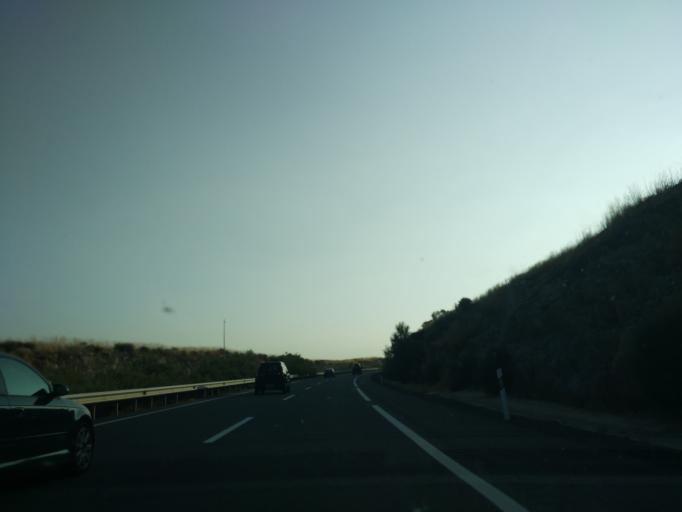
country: ES
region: Castille and Leon
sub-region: Provincia de Avila
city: Mediana de Voltoya
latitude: 40.7034
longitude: -4.5668
